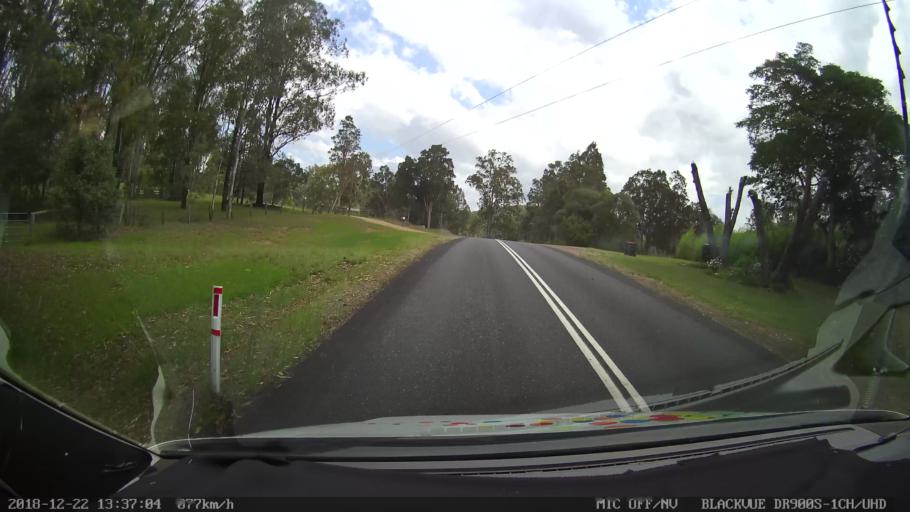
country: AU
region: New South Wales
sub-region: Clarence Valley
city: Coutts Crossing
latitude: -29.8862
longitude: 152.7899
